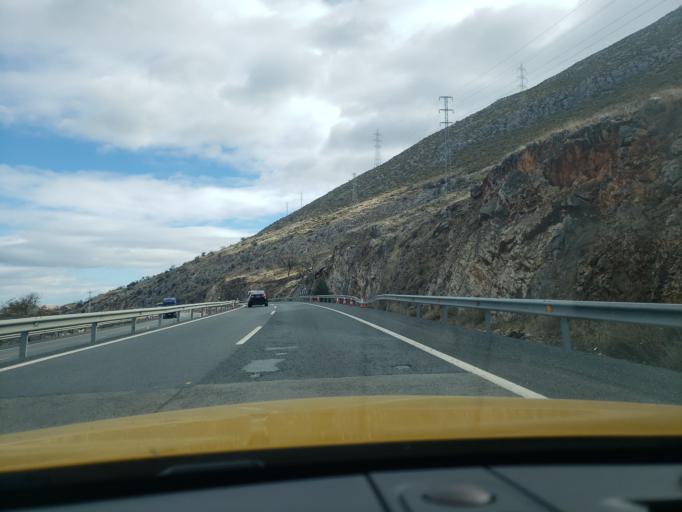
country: ES
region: Andalusia
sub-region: Provincia de Granada
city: Loja
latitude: 37.1596
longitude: -4.1484
